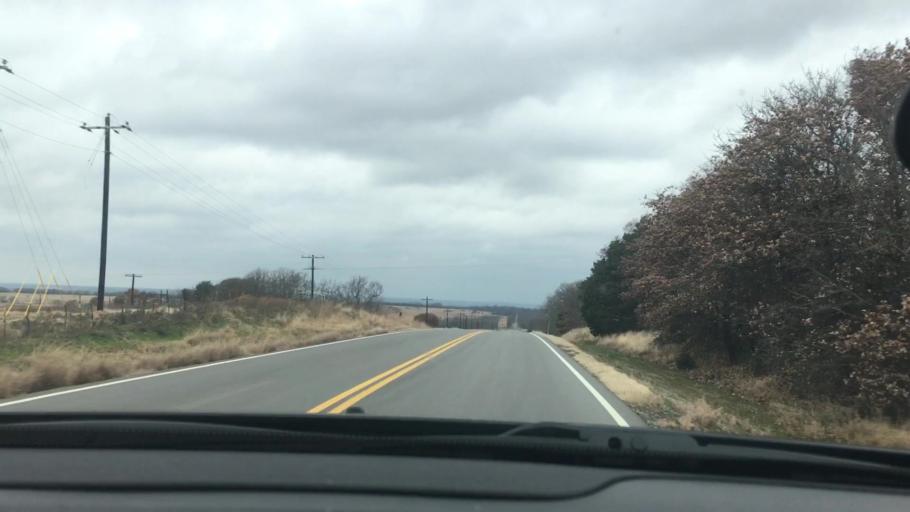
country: US
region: Oklahoma
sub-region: Atoka County
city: Atoka
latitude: 34.3749
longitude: -96.2487
